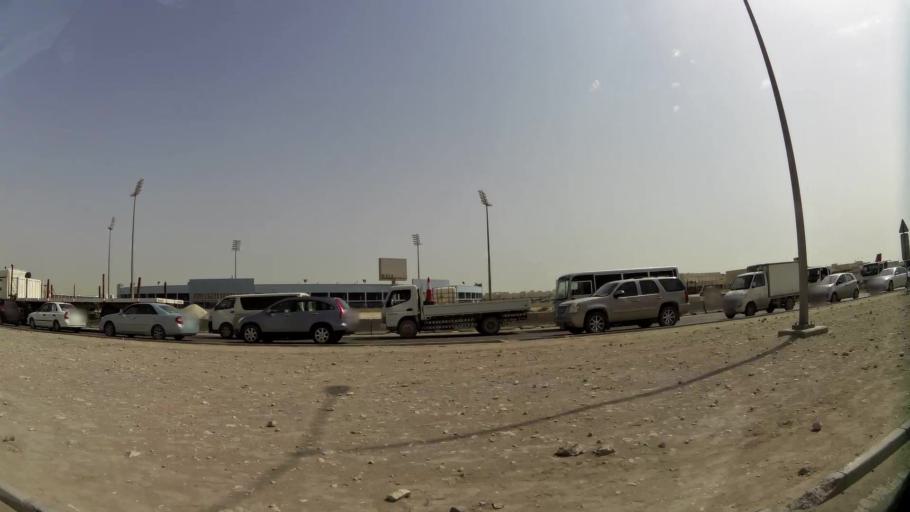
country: QA
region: Al Wakrah
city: Al Wukayr
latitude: 25.1875
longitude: 51.4587
